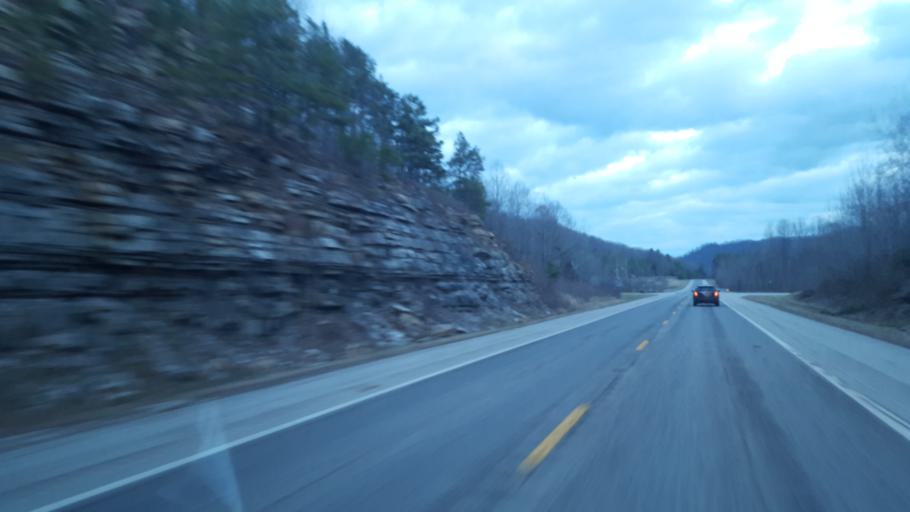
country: US
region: Kentucky
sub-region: Lewis County
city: Vanceburg
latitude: 38.5926
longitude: -83.2042
